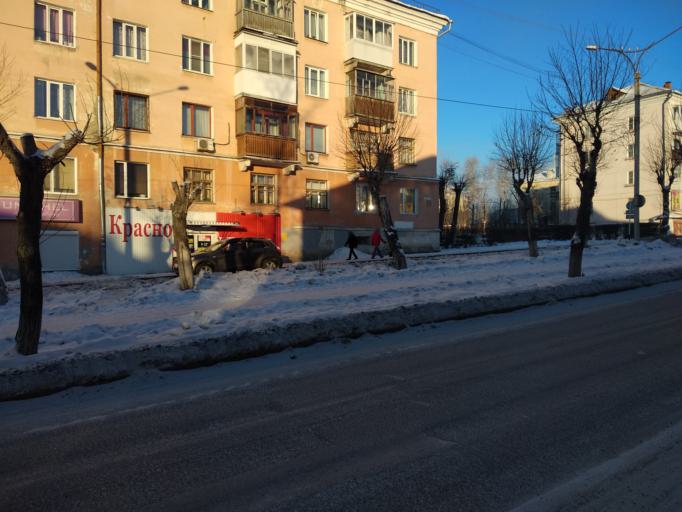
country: RU
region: Sverdlovsk
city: Krasnotur'insk
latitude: 59.7663
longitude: 60.1972
